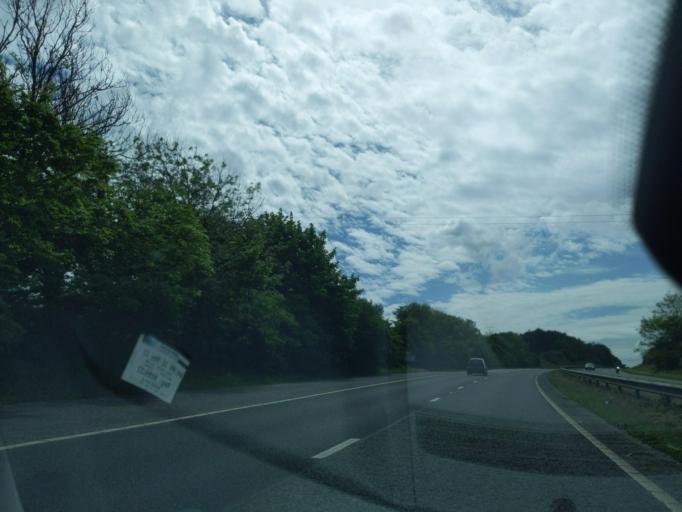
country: GB
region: England
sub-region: Cornwall
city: St. Day
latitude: 50.2535
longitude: -5.2031
